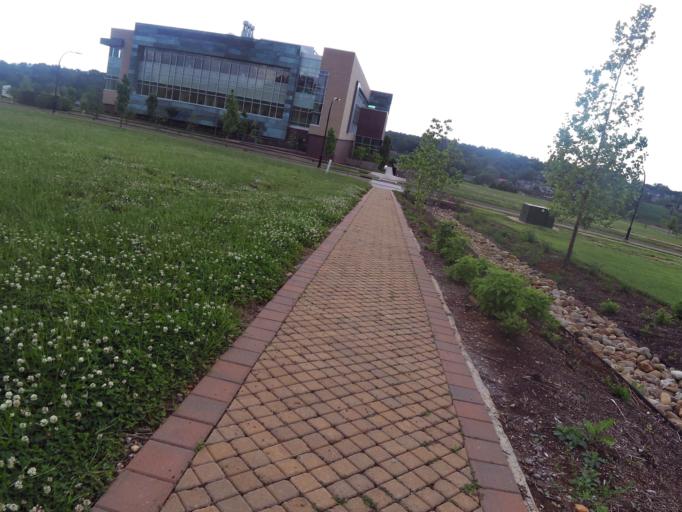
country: US
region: Tennessee
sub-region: Knox County
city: Knoxville
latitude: 35.9428
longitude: -83.9511
